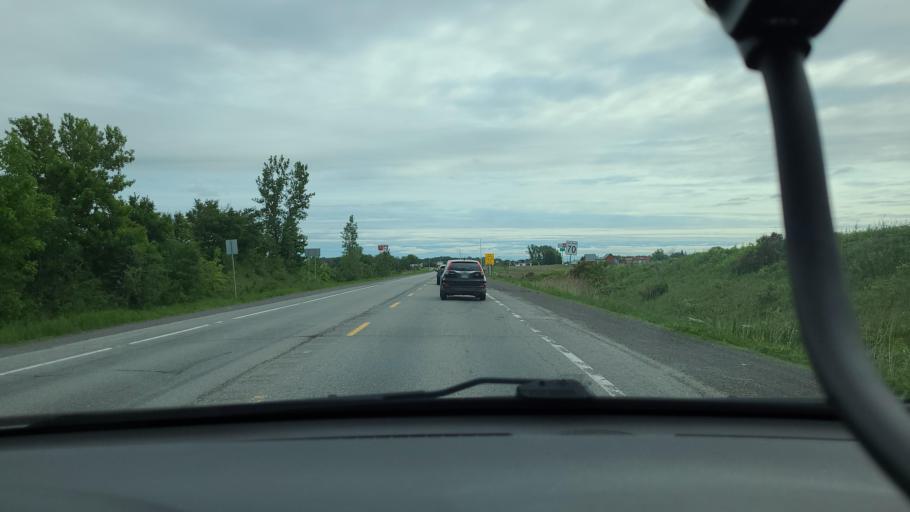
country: CA
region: Quebec
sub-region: Lanaudiere
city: Saint-Jacques
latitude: 45.9496
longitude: -73.5851
